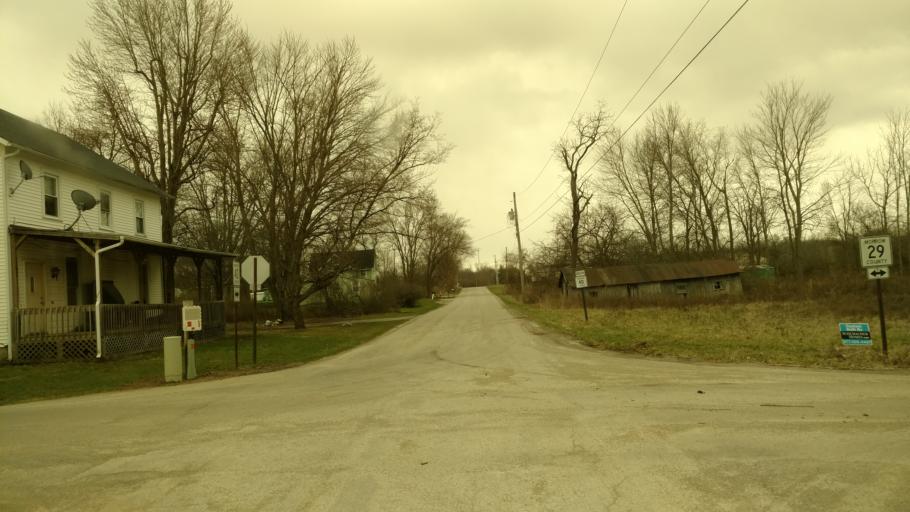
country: US
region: Ohio
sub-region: Crawford County
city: Galion
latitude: 40.6396
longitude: -82.7849
